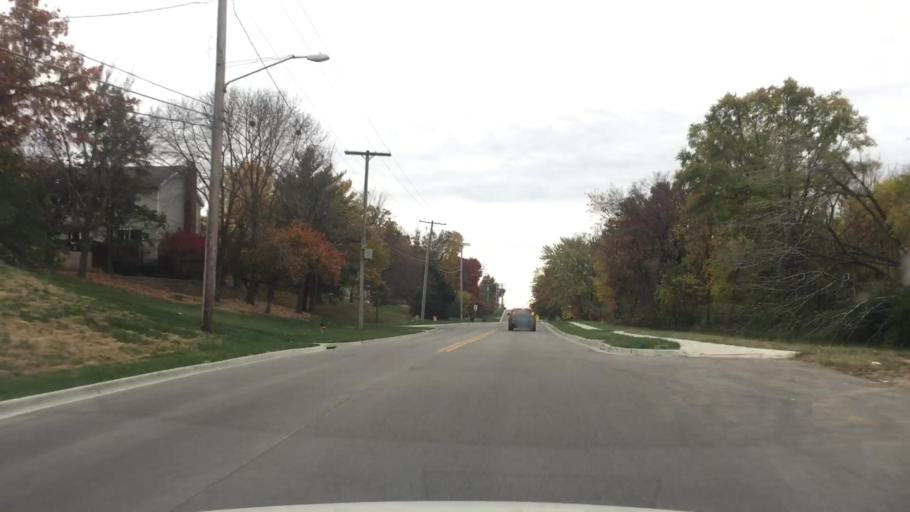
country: US
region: Kansas
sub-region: Johnson County
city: Shawnee
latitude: 39.0427
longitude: -94.7239
